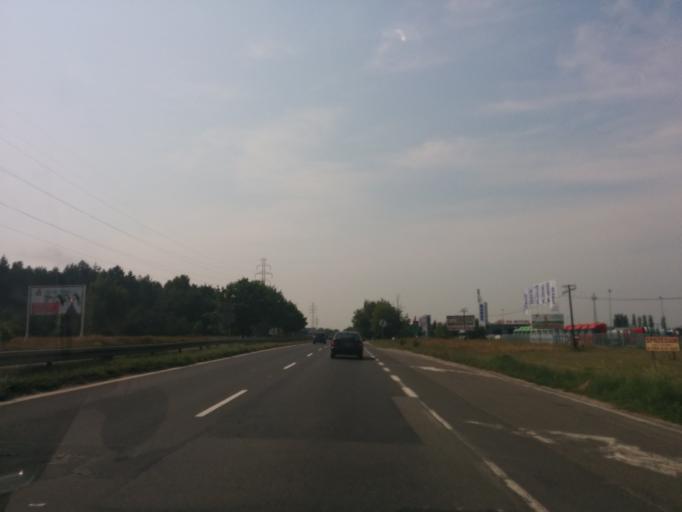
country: PL
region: Masovian Voivodeship
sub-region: Powiat pruszkowski
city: Nadarzyn
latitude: 52.1019
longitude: 20.8264
